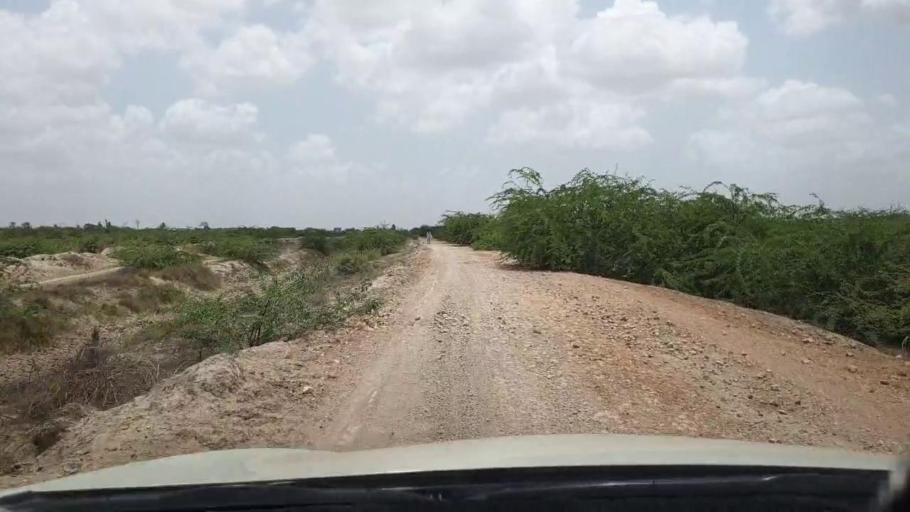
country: PK
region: Sindh
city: Kadhan
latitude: 24.3843
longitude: 68.9317
